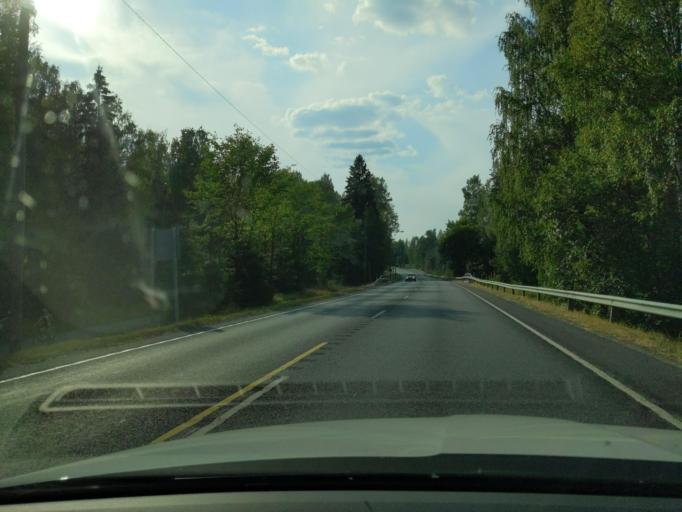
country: FI
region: Paijanne Tavastia
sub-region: Lahti
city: Asikkala
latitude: 61.1682
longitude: 25.5578
